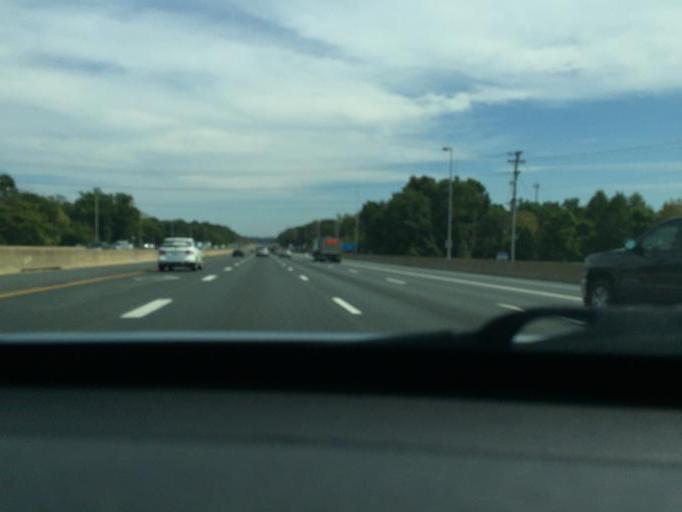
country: US
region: Virginia
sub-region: Prince William County
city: Sudley
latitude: 38.8071
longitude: -77.4977
